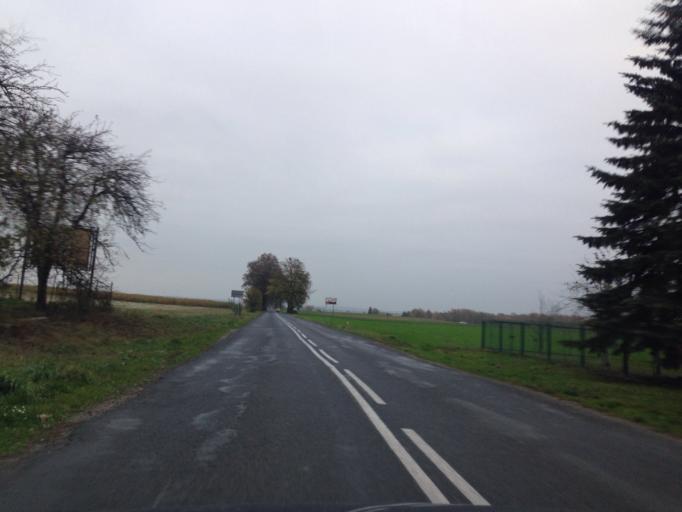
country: PL
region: Kujawsko-Pomorskie
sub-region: Powiat brodnicki
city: Bartniczka
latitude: 53.2394
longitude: 19.5051
